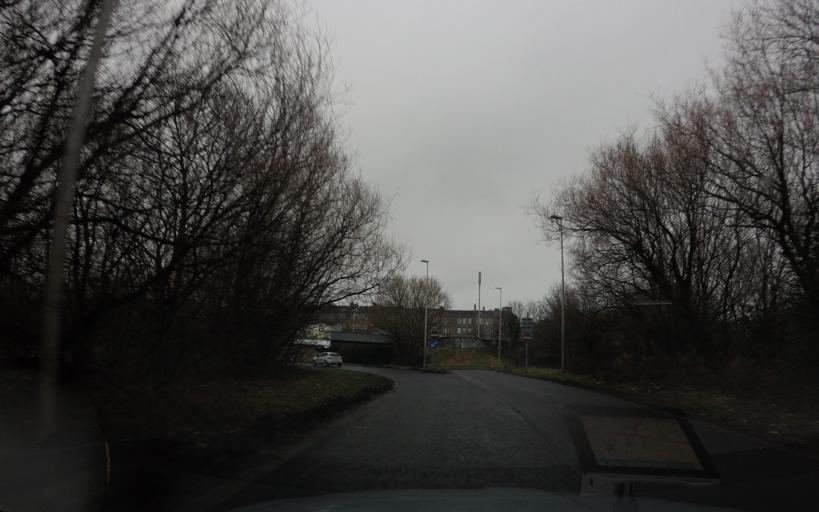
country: GB
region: Scotland
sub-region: Edinburgh
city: Edinburgh
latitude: 55.9406
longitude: -3.2228
